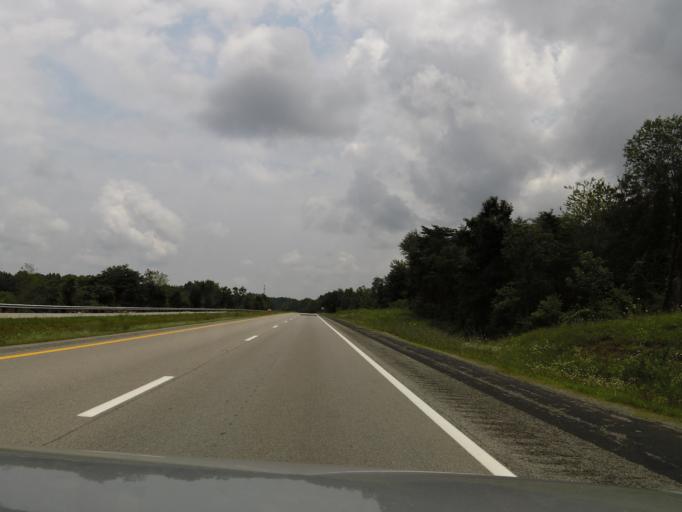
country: US
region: Kentucky
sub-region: Grayson County
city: Leitchfield
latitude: 37.5517
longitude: -86.0996
